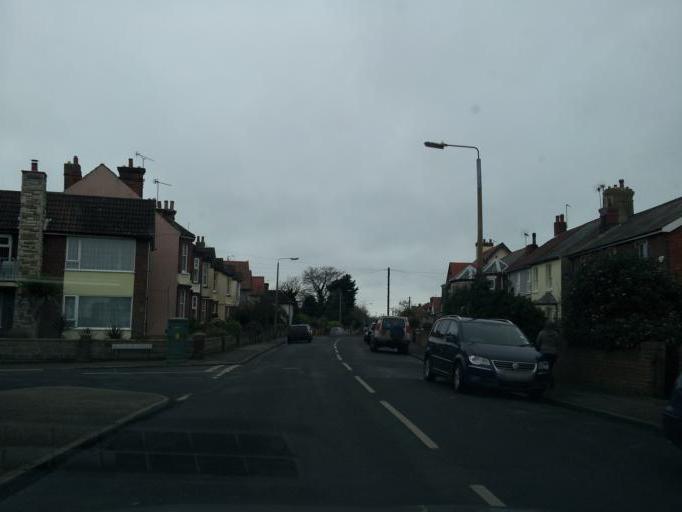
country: GB
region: England
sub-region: Essex
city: Dovercourt
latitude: 51.9323
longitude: 1.2739
